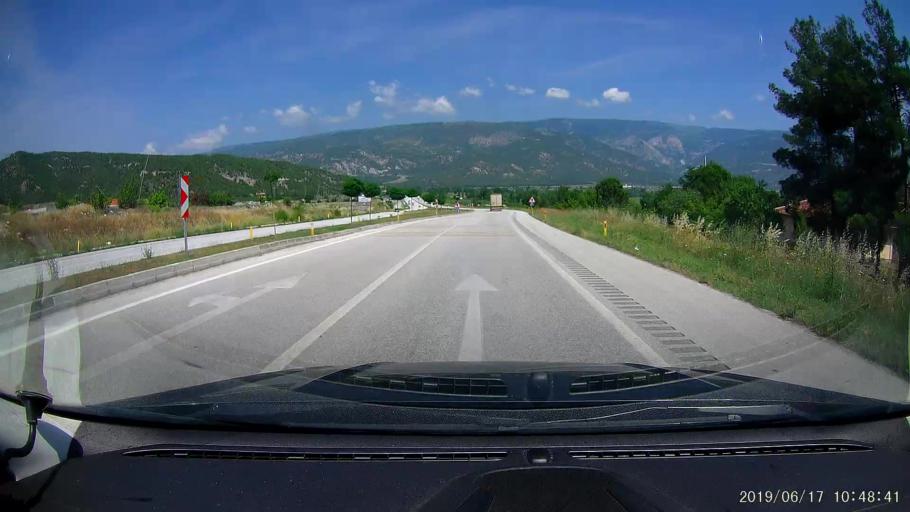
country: TR
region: Corum
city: Hacihamza
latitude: 41.0921
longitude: 34.4247
